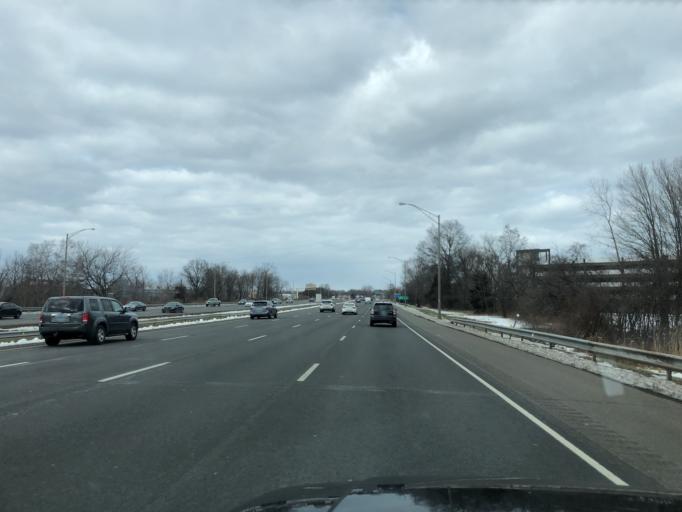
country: US
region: Connecticut
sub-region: New Haven County
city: North Haven
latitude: 41.3362
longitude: -72.8744
